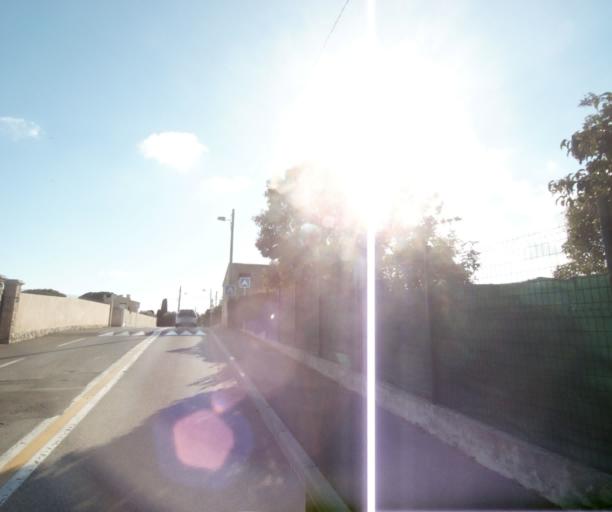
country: FR
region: Provence-Alpes-Cote d'Azur
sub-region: Departement des Alpes-Maritimes
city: Biot
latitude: 43.6014
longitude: 7.1063
